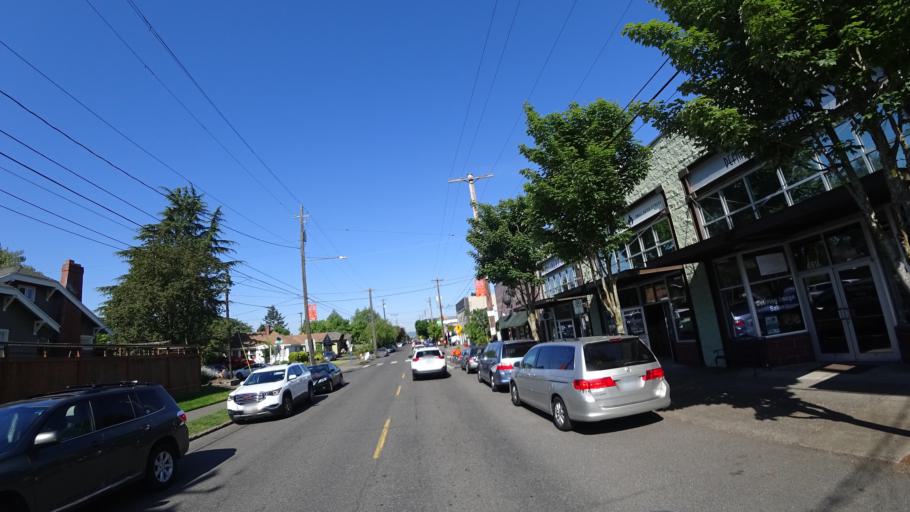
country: US
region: Oregon
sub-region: Multnomah County
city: Portland
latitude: 45.5483
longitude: -122.6133
